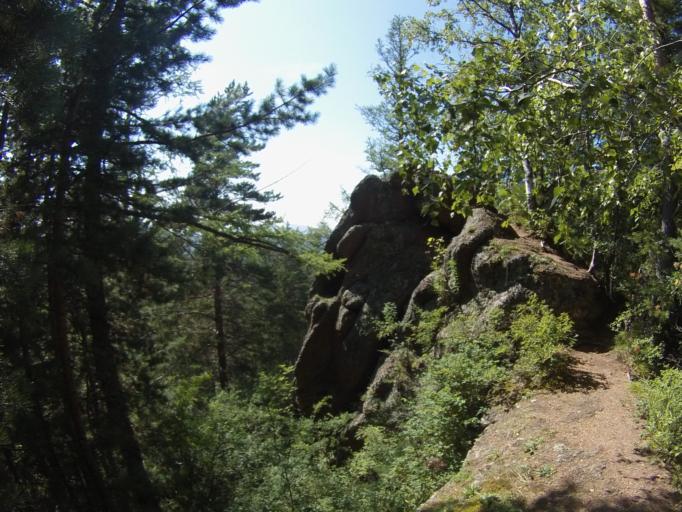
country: RU
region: Krasnoyarskiy
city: Krasnoyarsk
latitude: 55.9323
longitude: 92.7585
